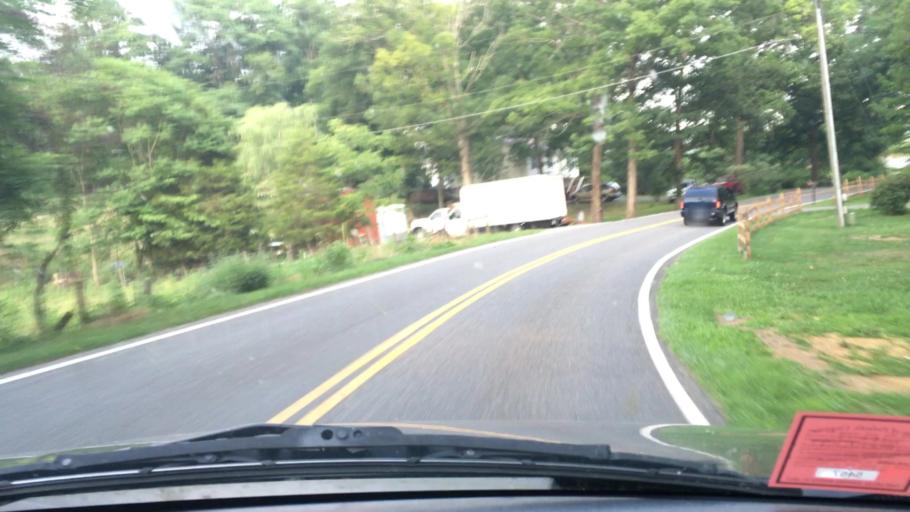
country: US
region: Virginia
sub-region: Pulaski County
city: Dublin
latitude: 37.0555
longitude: -80.6971
